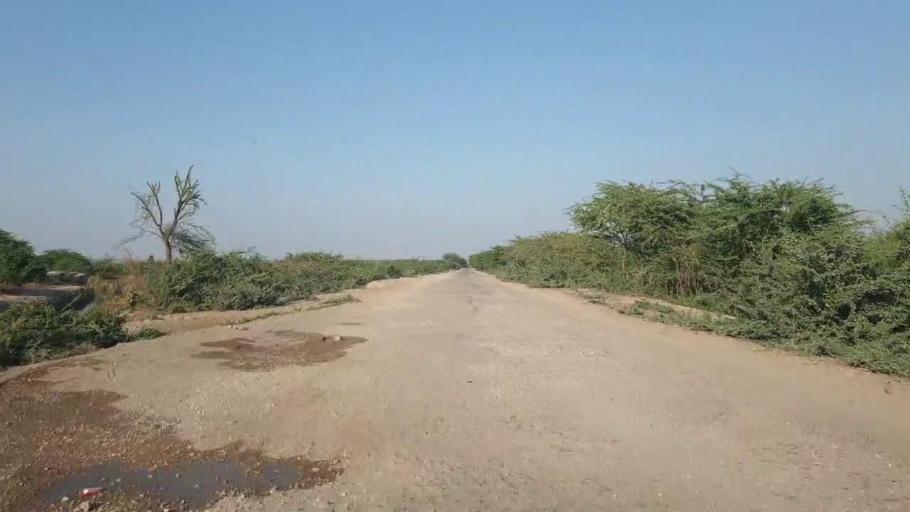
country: PK
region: Sindh
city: Chor
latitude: 25.5501
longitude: 69.7876
